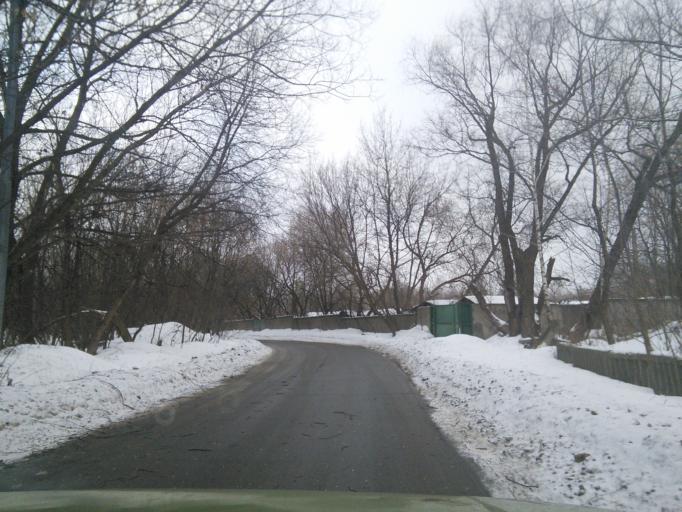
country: RU
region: Moskovskaya
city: Fili
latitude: 55.7568
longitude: 37.4729
